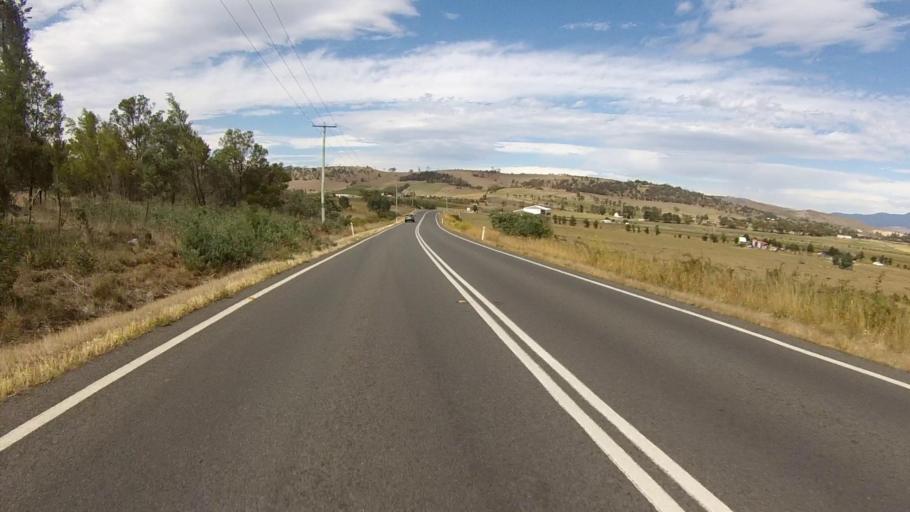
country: AU
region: Tasmania
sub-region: Brighton
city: Old Beach
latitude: -42.6849
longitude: 147.3515
